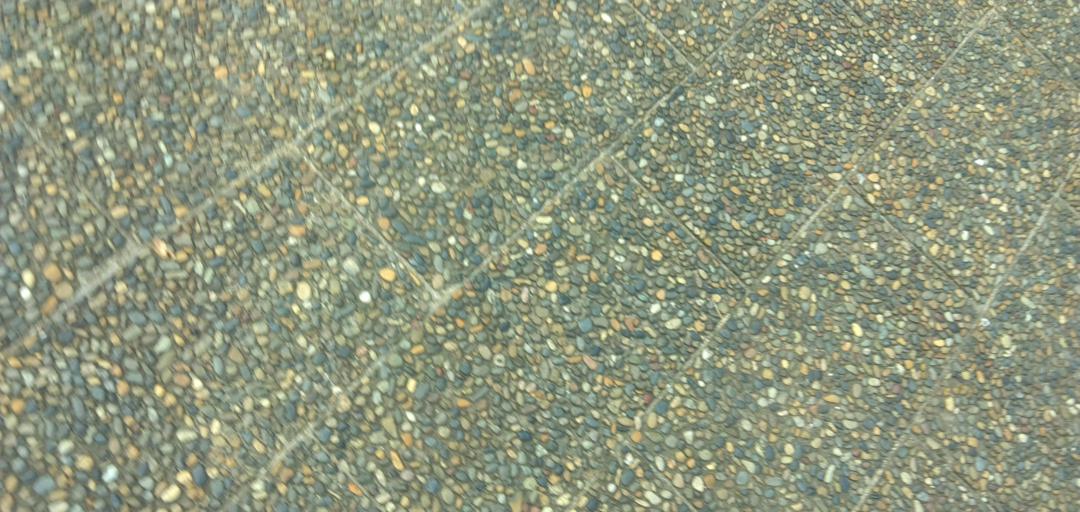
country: JP
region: Osaka
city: Yao
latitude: 34.6293
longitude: 135.5783
